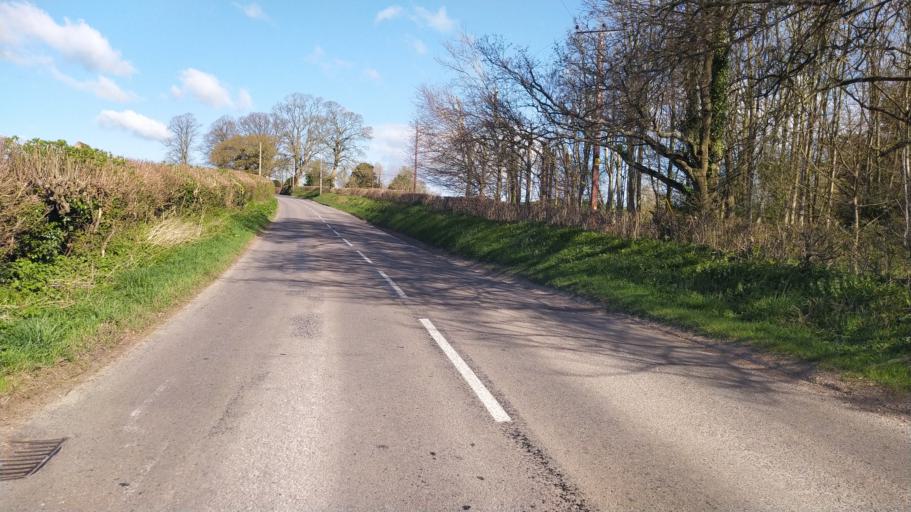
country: GB
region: England
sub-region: Dorset
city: Sturminster Newton
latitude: 50.9612
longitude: -2.3125
